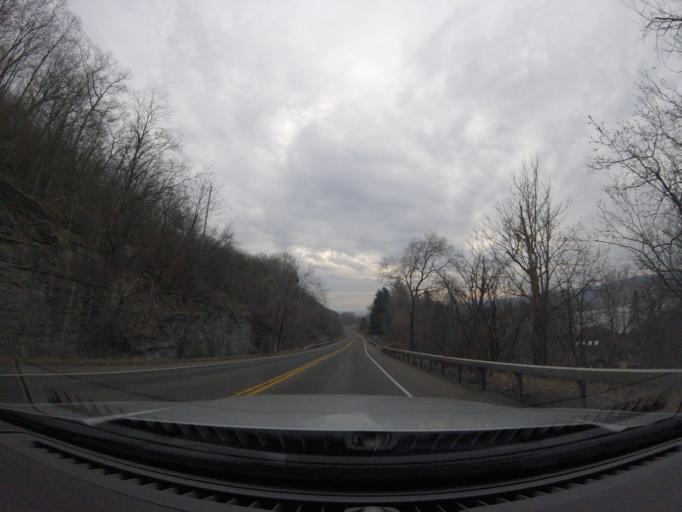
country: US
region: New York
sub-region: Schuyler County
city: Watkins Glen
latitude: 42.3921
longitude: -76.8561
